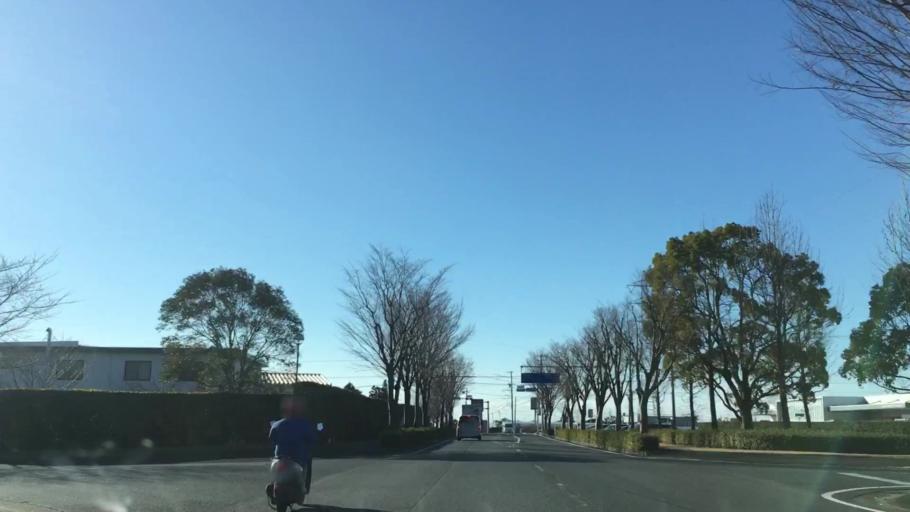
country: JP
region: Shizuoka
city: Hamakita
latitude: 34.8047
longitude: 137.7448
